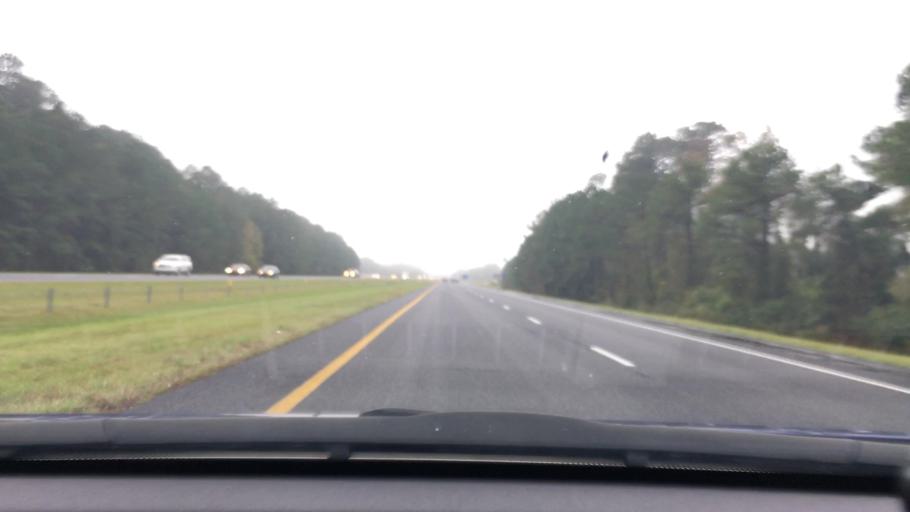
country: US
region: South Carolina
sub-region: Florence County
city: Timmonsville
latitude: 34.2072
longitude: -80.0457
